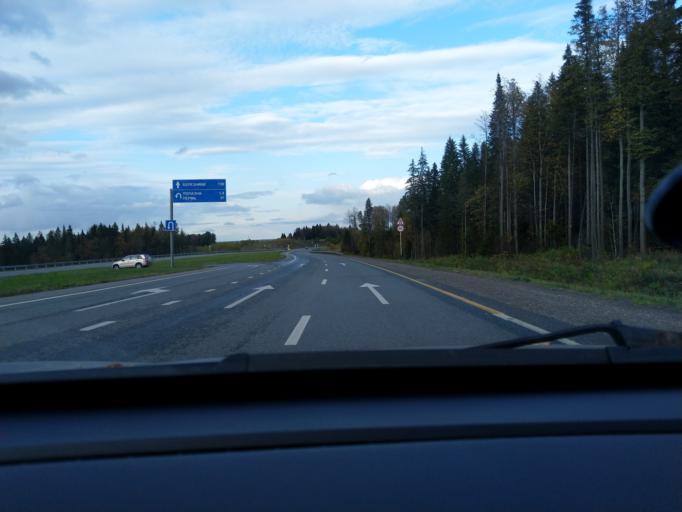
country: RU
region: Perm
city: Polazna
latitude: 58.2759
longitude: 56.4211
